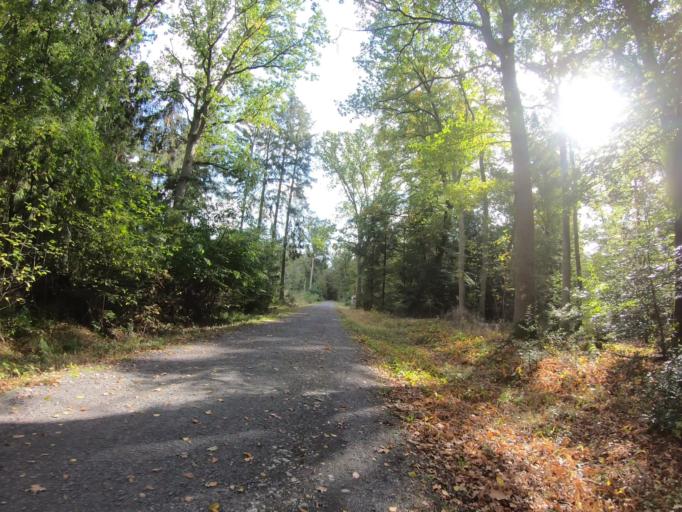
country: DE
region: Lower Saxony
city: Isenbuttel
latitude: 52.4544
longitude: 10.5705
